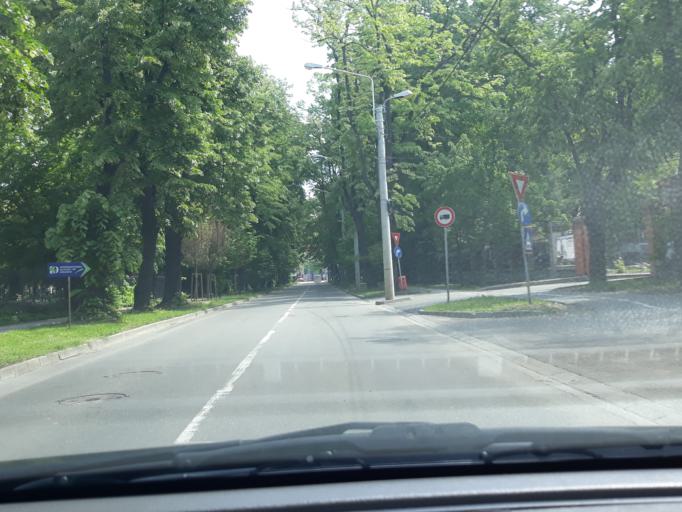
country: RO
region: Bihor
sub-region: Comuna Biharea
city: Oradea
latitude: 47.0504
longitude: 21.9223
